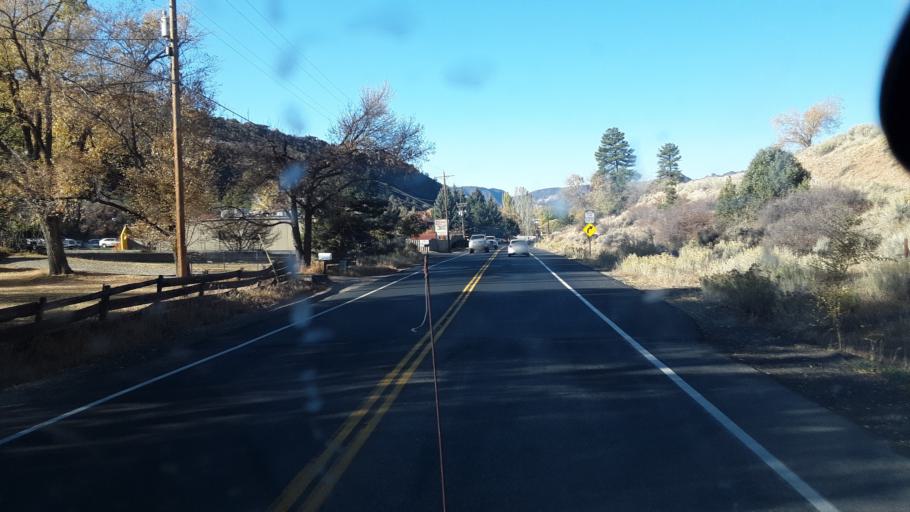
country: US
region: Colorado
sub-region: La Plata County
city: Durango
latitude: 37.2993
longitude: -107.8442
